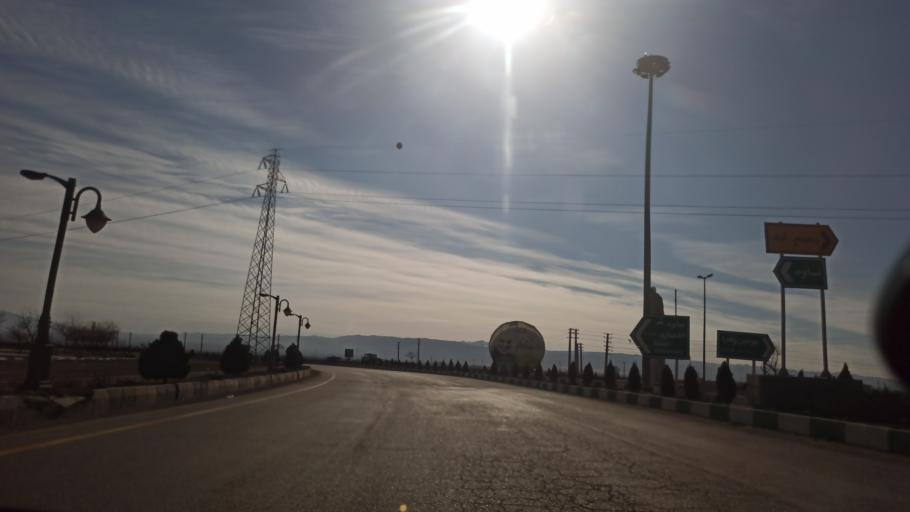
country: IR
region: Qazvin
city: Bu'in Zahra
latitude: 35.7673
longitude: 50.0832
